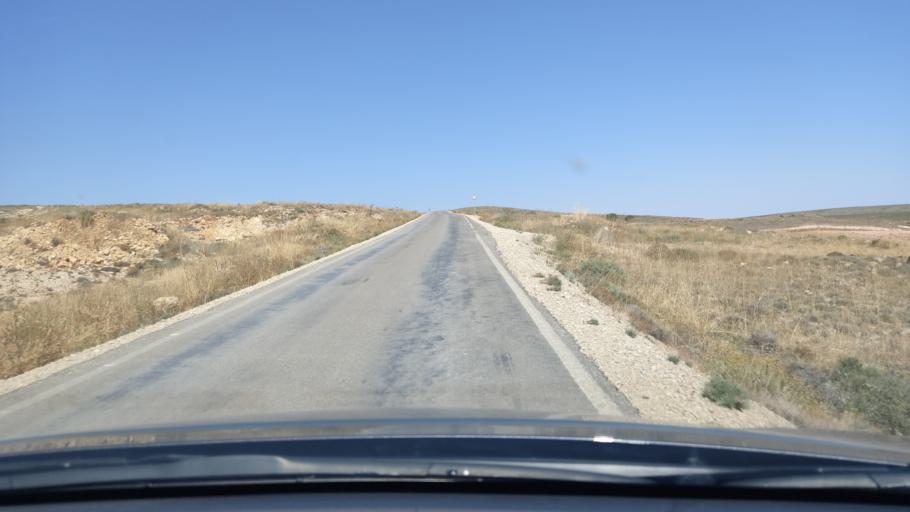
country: ES
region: Aragon
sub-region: Provincia de Teruel
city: Monforte de Moyuela
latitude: 41.0405
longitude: -0.9831
